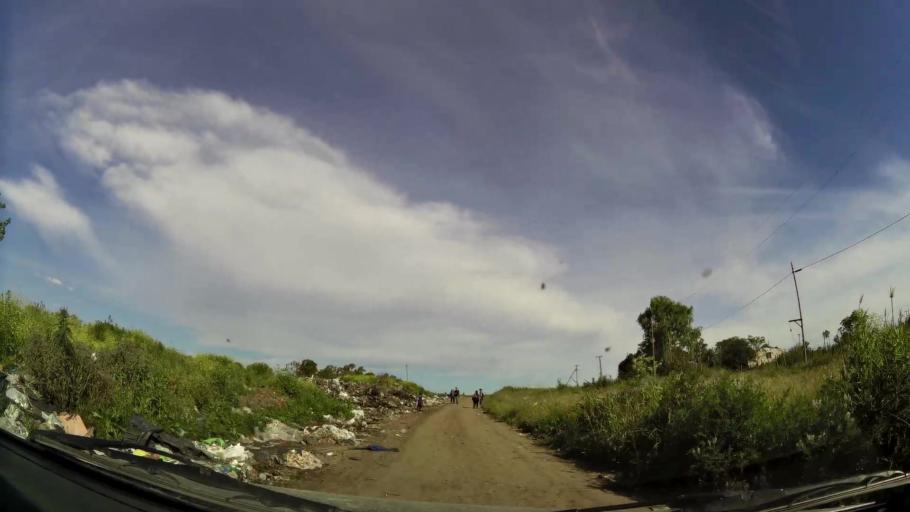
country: AR
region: Buenos Aires
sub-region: Partido de Almirante Brown
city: Adrogue
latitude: -34.8247
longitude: -58.3379
